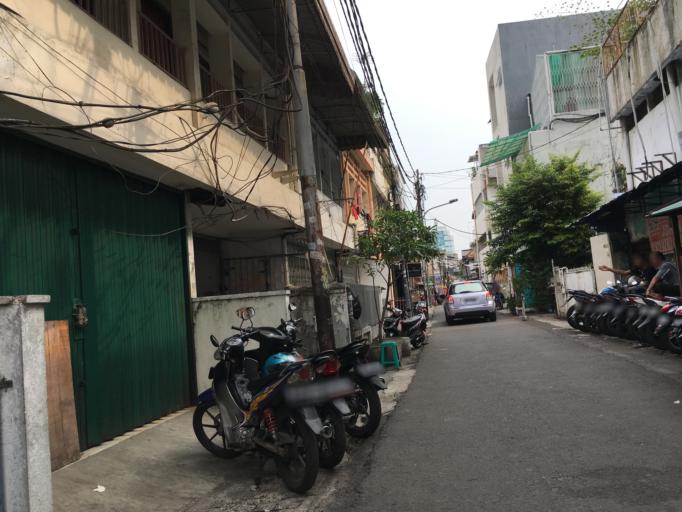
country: ID
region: Jakarta Raya
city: Jakarta
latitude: -6.1632
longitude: 106.8343
